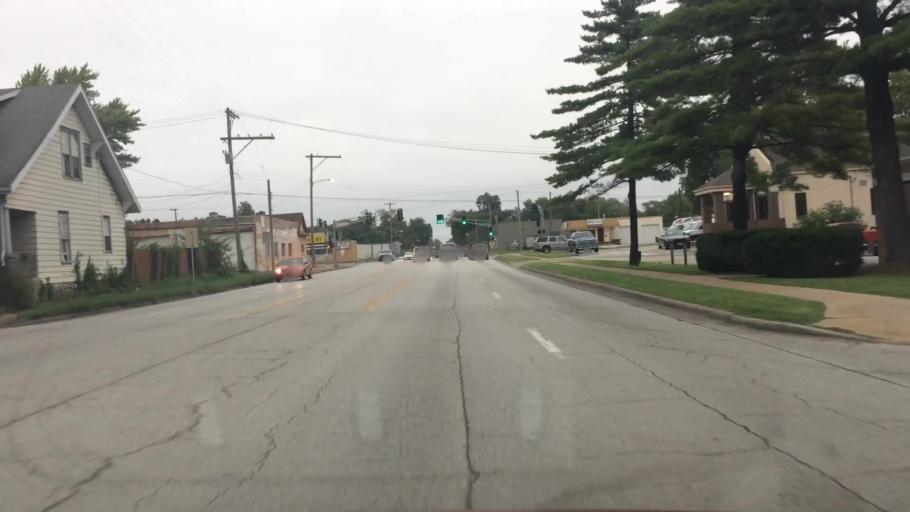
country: US
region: Missouri
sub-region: Greene County
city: Springfield
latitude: 37.2286
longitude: -93.2753
